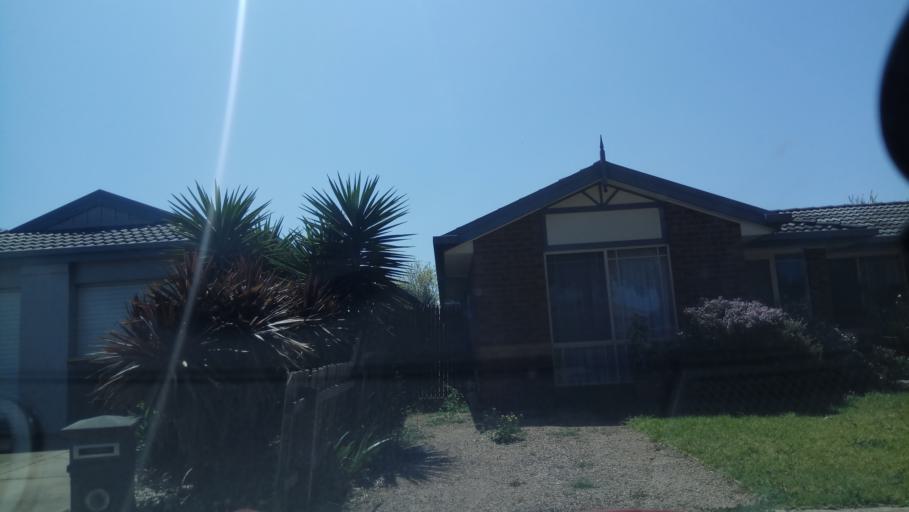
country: AU
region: Victoria
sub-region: Wyndham
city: Williams Landing
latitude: -37.8819
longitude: 144.7481
